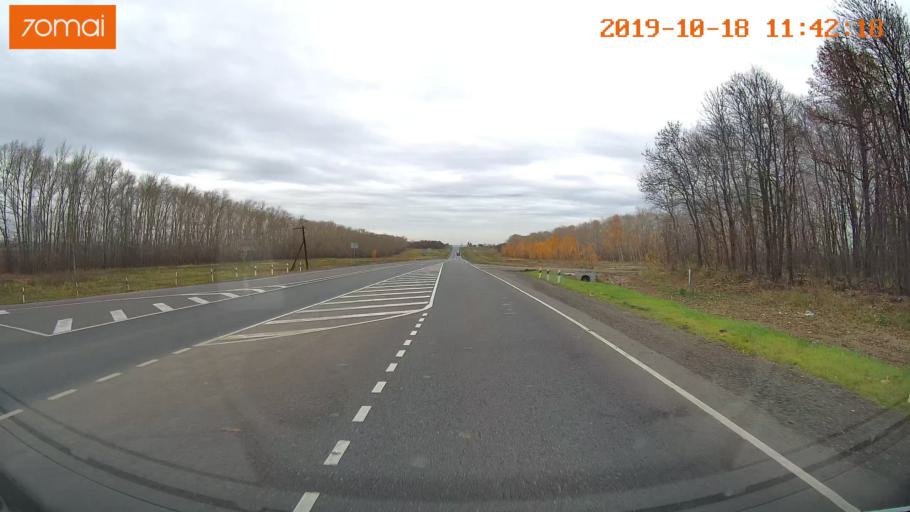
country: RU
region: Rjazan
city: Oktyabr'skiy
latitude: 54.1868
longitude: 38.9249
